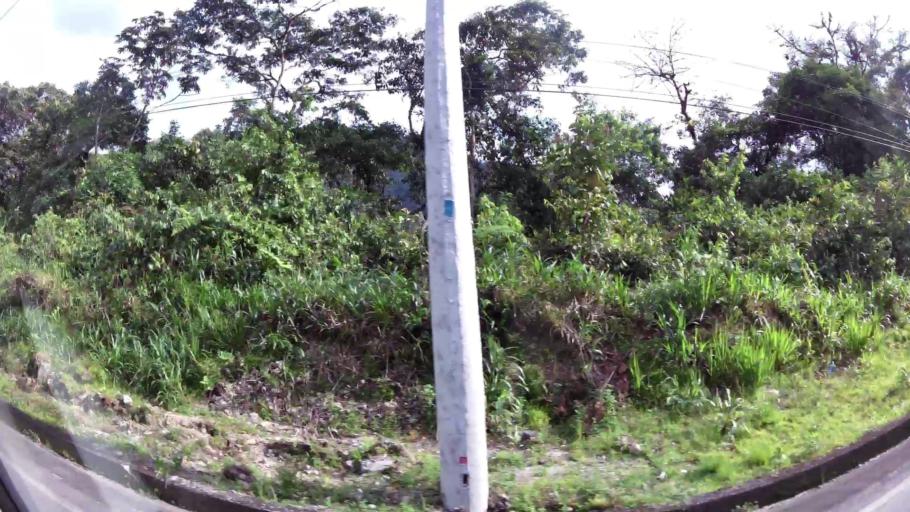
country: EC
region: Pastaza
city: Puyo
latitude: -1.4117
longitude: -78.1968
